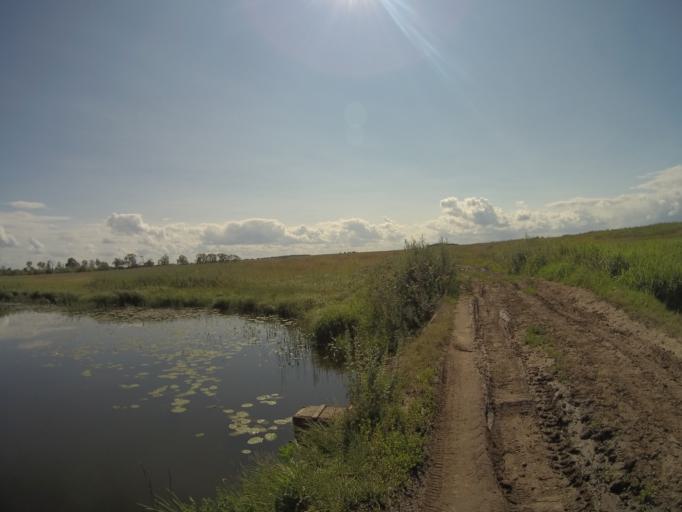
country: RU
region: Vladimir
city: Vladimir
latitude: 56.2785
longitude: 40.3447
